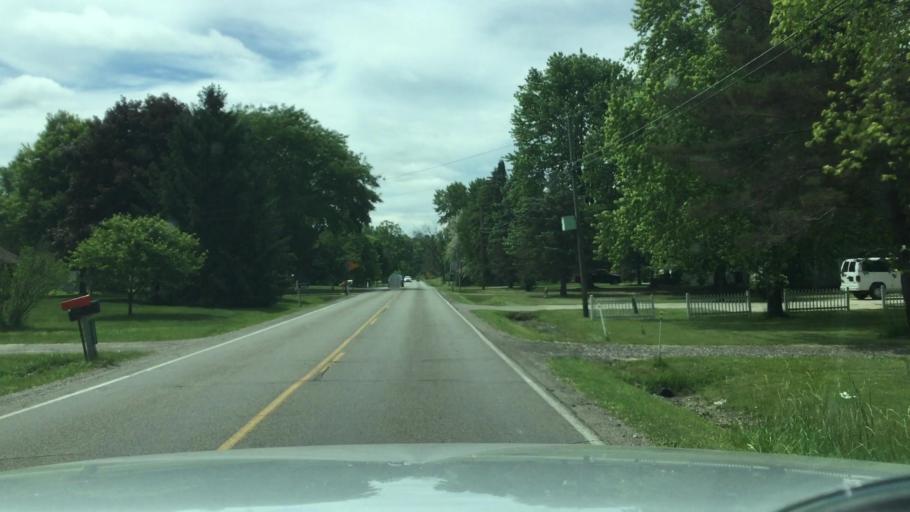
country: US
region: Michigan
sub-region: Genesee County
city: Clio
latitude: 43.1910
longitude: -83.7744
